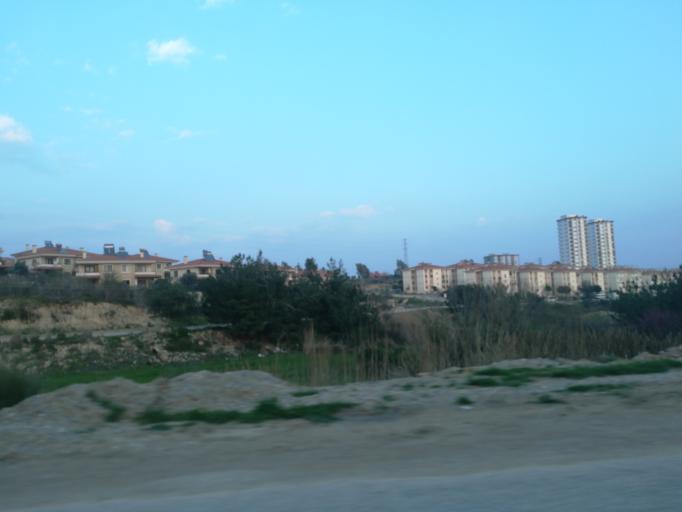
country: TR
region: Adana
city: Adana
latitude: 37.0817
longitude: 35.4094
